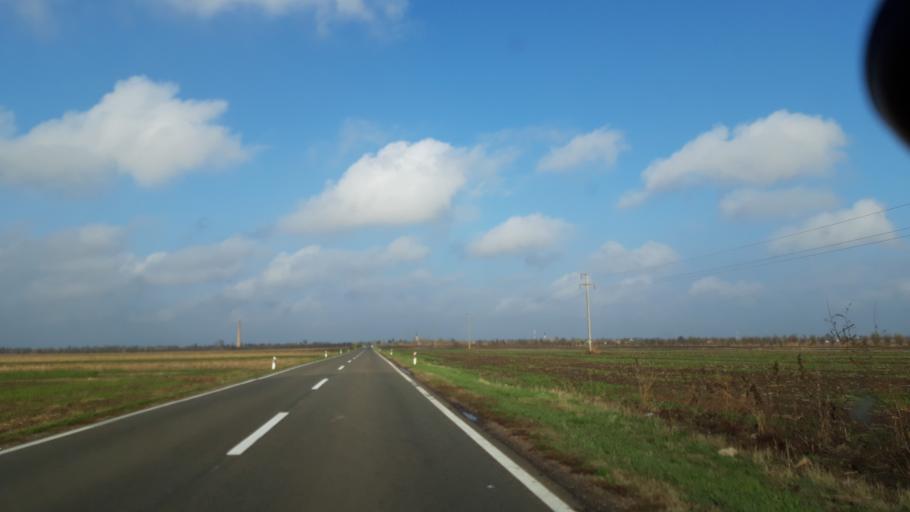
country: RS
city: Ostojicevo
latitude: 45.8735
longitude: 20.1651
